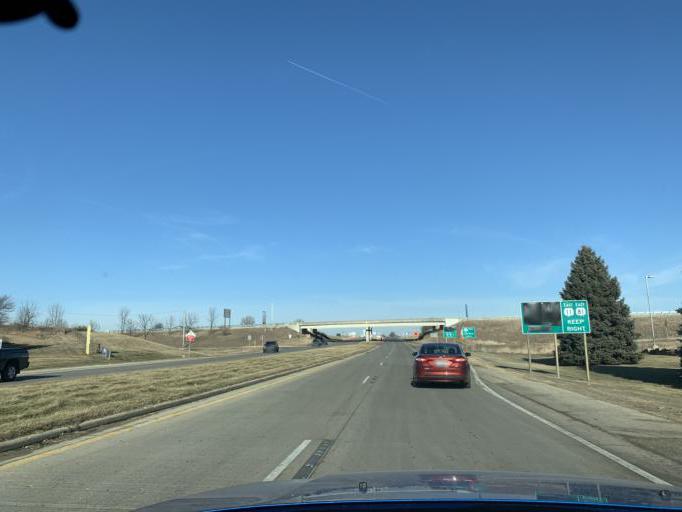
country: US
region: Wisconsin
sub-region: Green County
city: Monroe
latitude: 42.6153
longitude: -89.6366
